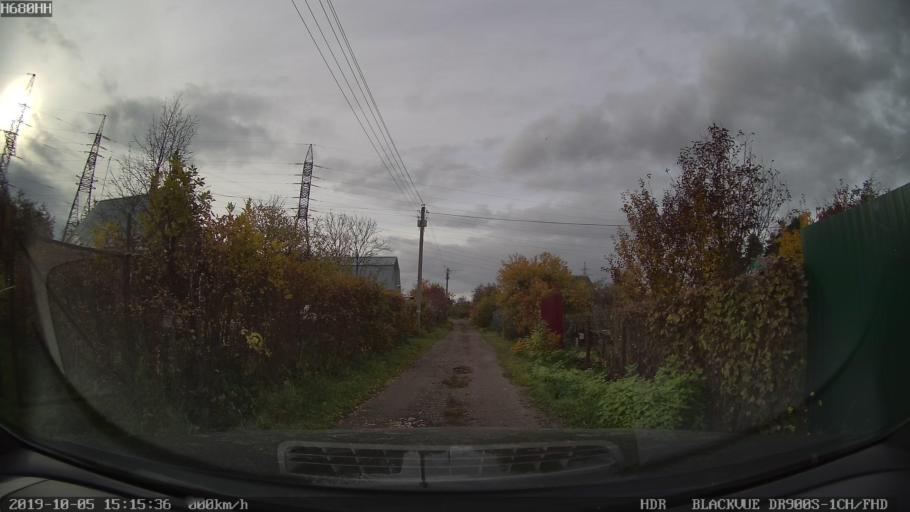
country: RU
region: Moskovskaya
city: Solnechnogorsk
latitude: 56.2140
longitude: 36.9105
